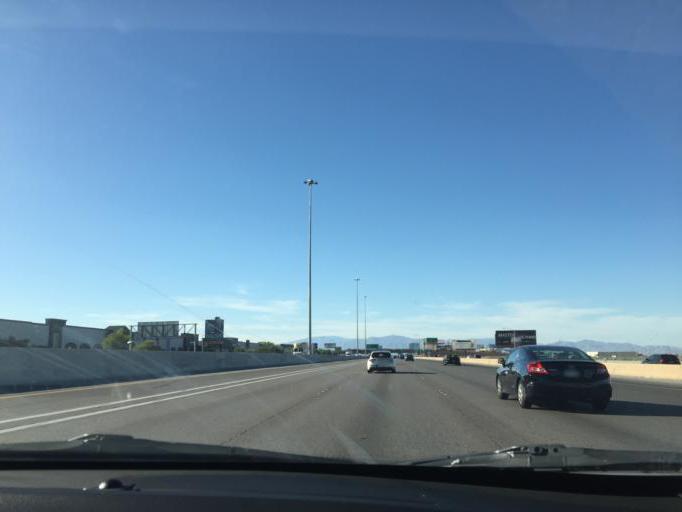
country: US
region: Nevada
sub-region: Clark County
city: Paradise
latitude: 36.0505
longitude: -115.1807
